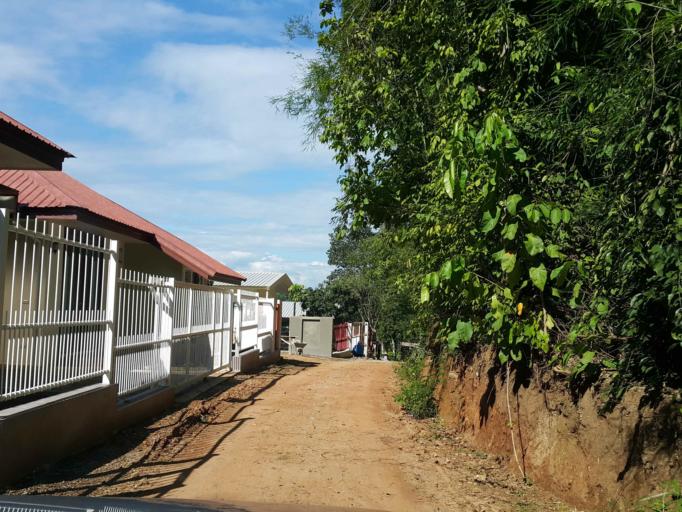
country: TH
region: Chiang Mai
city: Mae Taeng
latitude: 18.9673
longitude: 98.8957
